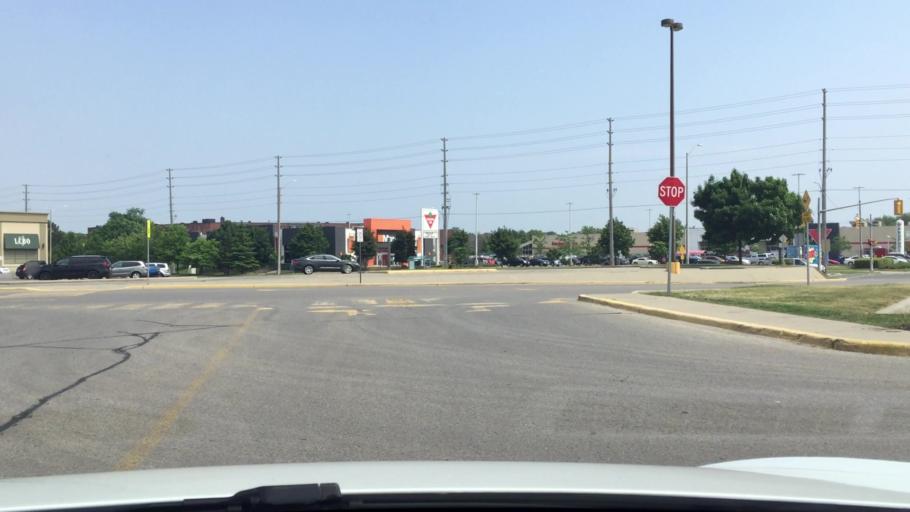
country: CA
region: Ontario
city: Oshawa
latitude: 43.8875
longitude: -78.8778
